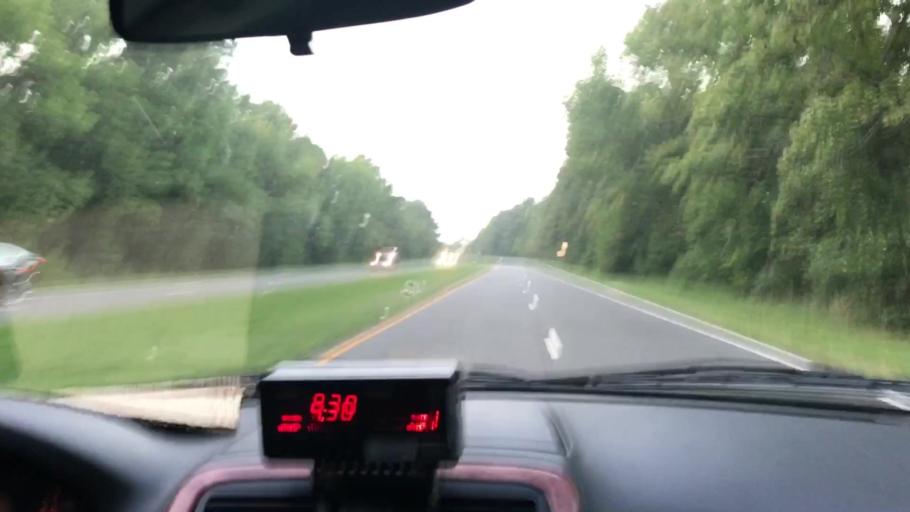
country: US
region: Virginia
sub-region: City of Hampton
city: Hampton
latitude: 37.0588
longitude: -76.3661
